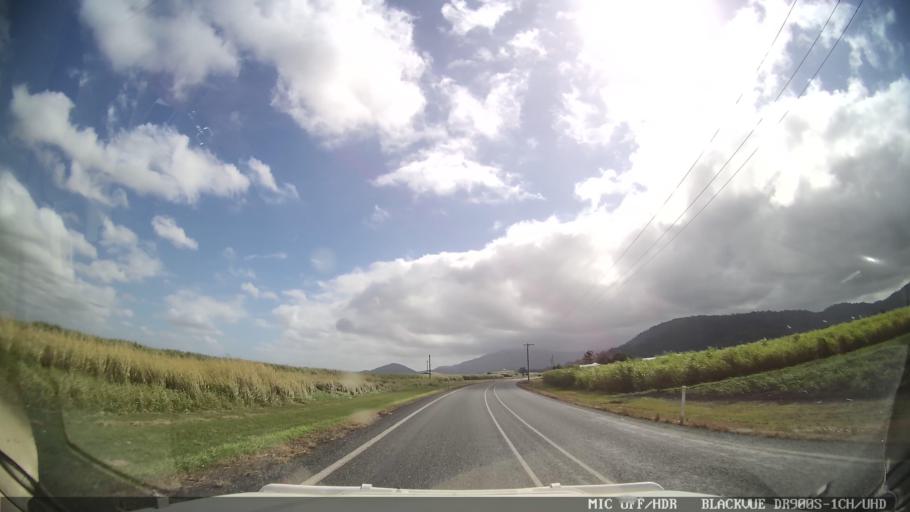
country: AU
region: Queensland
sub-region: Whitsunday
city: Red Hill
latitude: -20.3449
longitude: 148.5527
